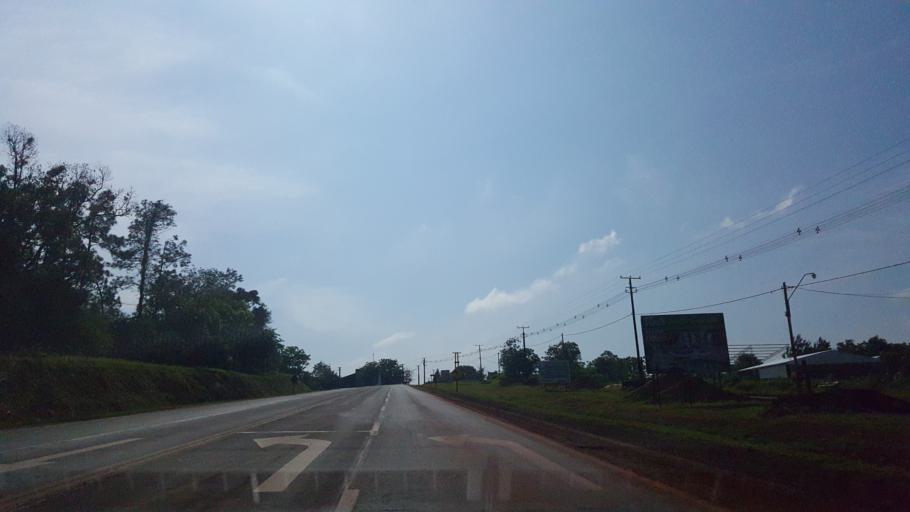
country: AR
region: Misiones
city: Capiovi
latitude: -26.9354
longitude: -55.0646
